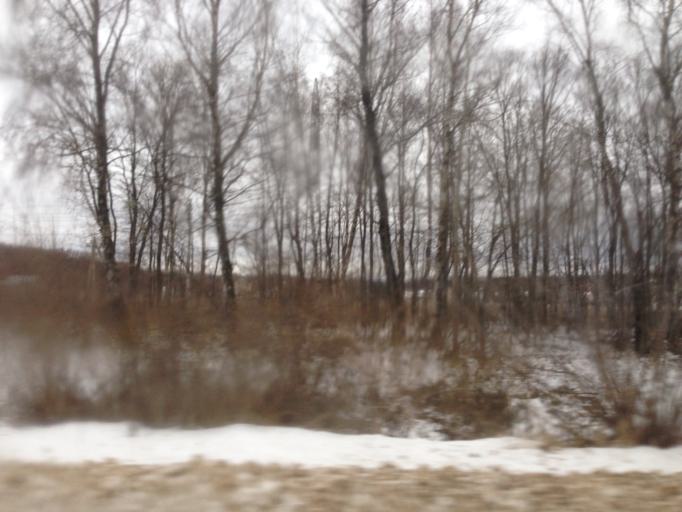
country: RU
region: Tula
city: Skuratovskiy
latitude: 54.1231
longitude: 37.6932
